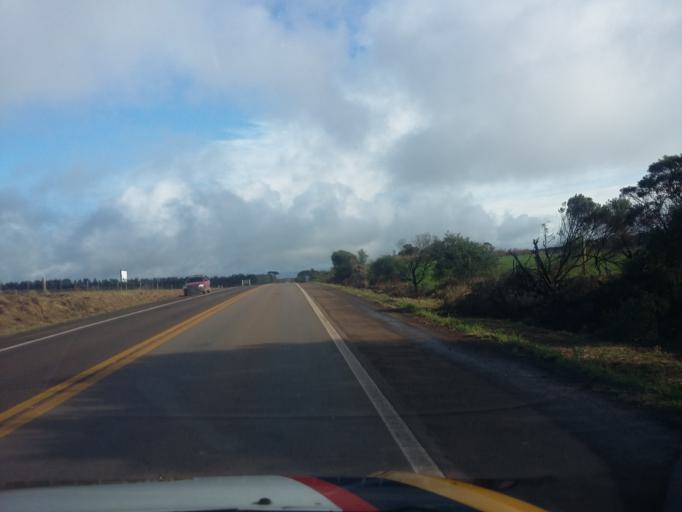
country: BR
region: Rio Grande do Sul
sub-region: Vacaria
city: Vacaria
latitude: -28.5324
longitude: -50.8023
